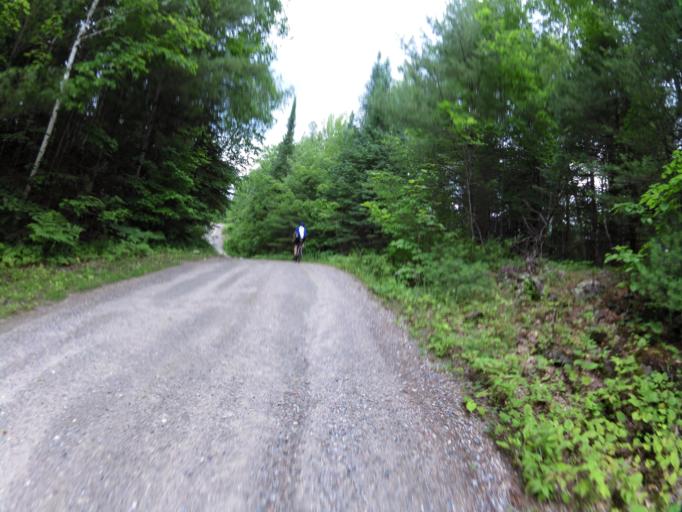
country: CA
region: Ontario
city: Perth
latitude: 45.0099
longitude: -76.5917
